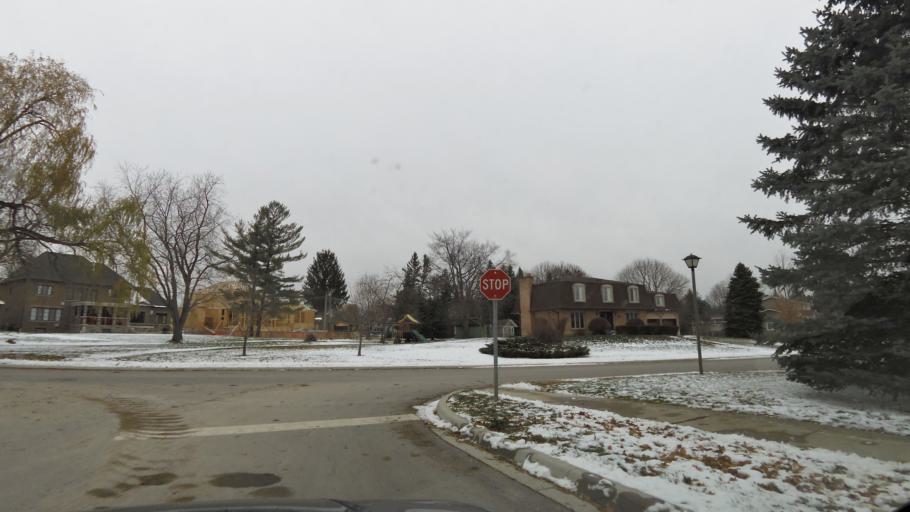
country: CA
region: Ontario
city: Vaughan
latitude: 43.8987
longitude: -79.6575
